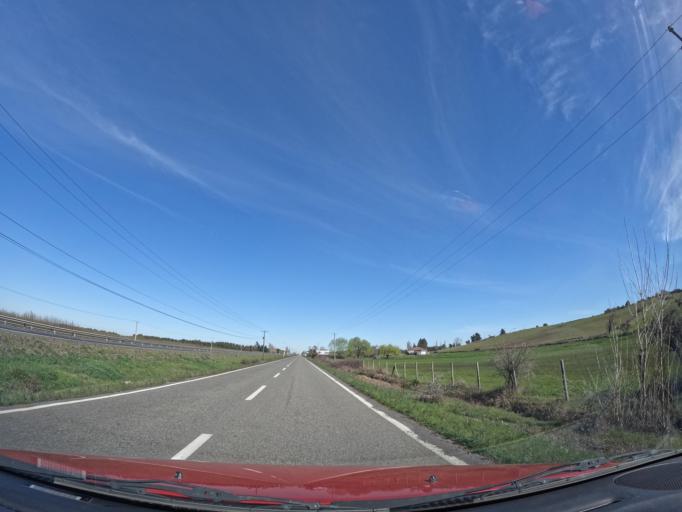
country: CL
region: Biobio
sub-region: Provincia de Biobio
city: Cabrero
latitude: -37.0125
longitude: -72.3649
